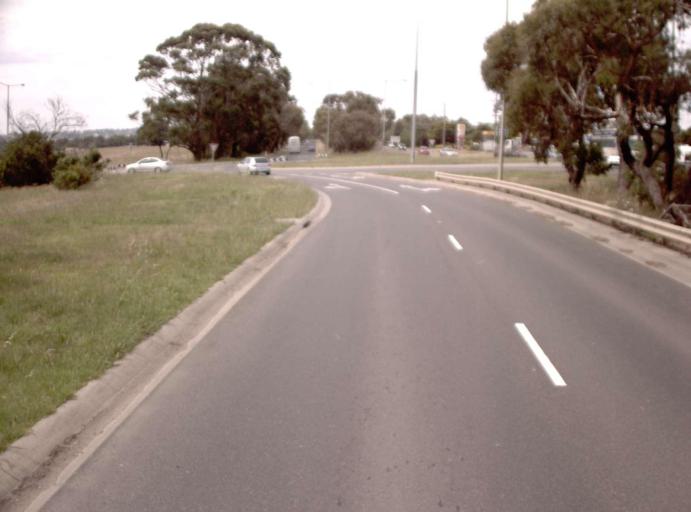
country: AU
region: Victoria
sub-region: Mornington Peninsula
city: Moorooduc
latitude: -38.2554
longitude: 145.0784
